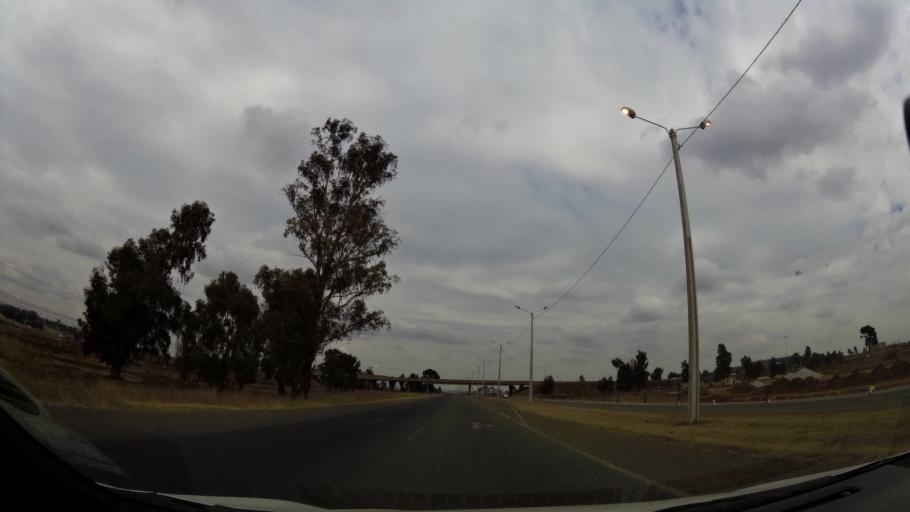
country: ZA
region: Gauteng
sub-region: Ekurhuleni Metropolitan Municipality
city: Germiston
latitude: -26.3621
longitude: 28.1183
